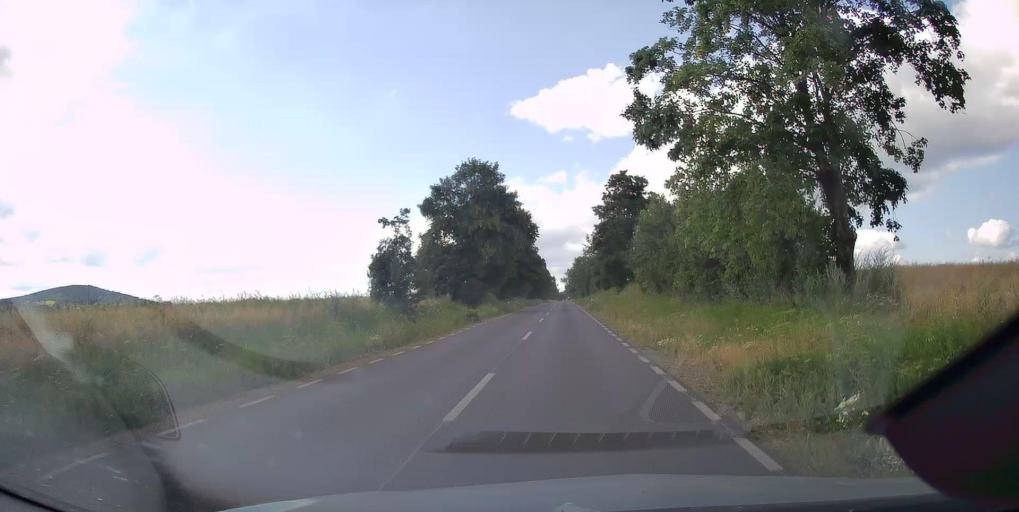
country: PL
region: Swietokrzyskie
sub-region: Powiat kielecki
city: Bodzentyn
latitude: 50.9250
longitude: 20.9850
